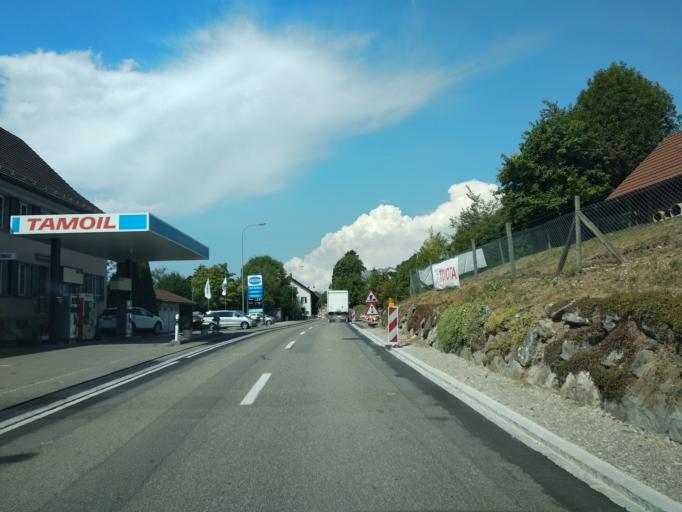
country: CH
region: Zurich
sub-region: Bezirk Winterthur
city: Sulz
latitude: 47.5947
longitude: 8.7873
